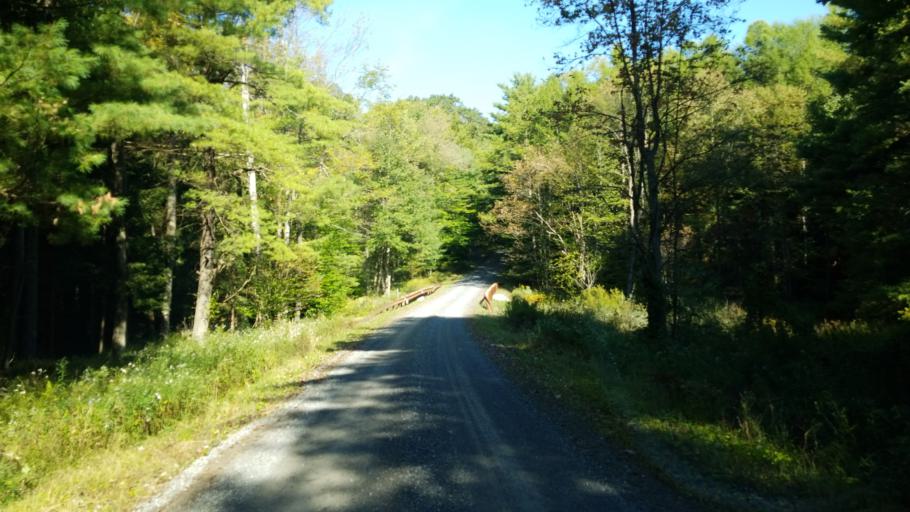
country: US
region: Pennsylvania
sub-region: Clearfield County
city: Treasure Lake
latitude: 41.1371
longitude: -78.5714
